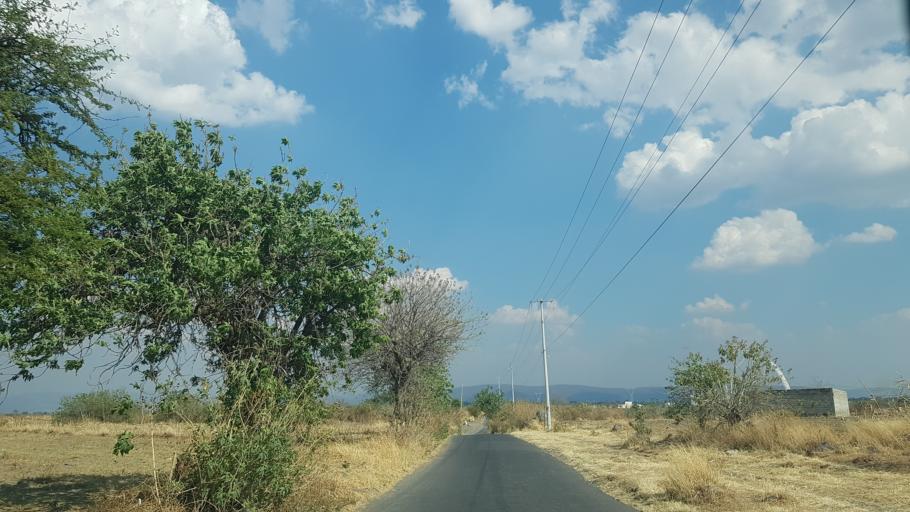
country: MX
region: Puebla
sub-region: Atlixco
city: Colonia Agricola de Ocotepec (Colonia San Jose)
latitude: 18.8897
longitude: -98.5035
